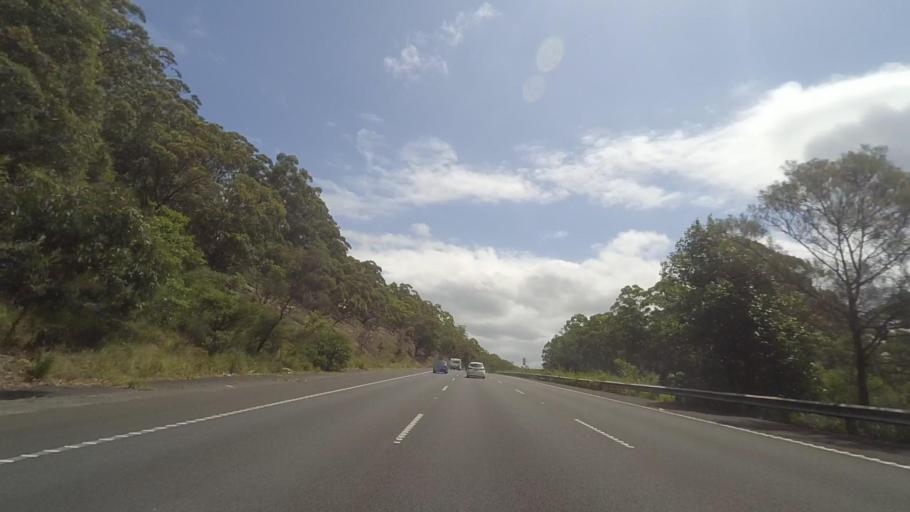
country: AU
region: New South Wales
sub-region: Gosford Shire
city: Lisarow
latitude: -33.3577
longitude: 151.3443
